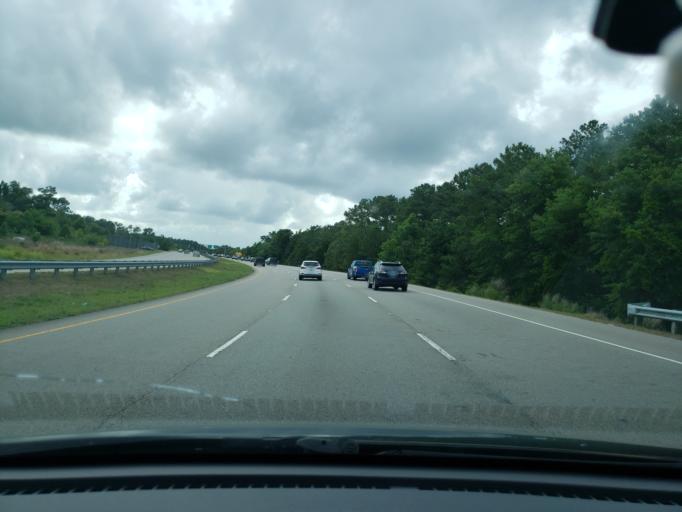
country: US
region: North Carolina
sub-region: New Hanover County
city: Wrightsboro
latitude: 34.2570
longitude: -77.9070
